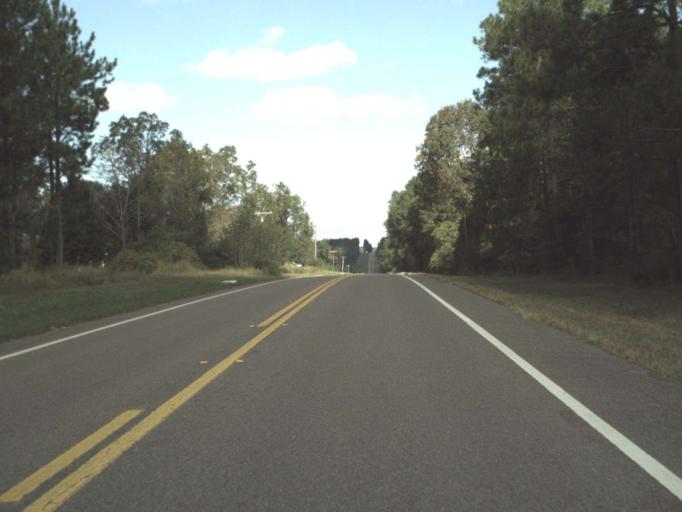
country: US
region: Florida
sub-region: Walton County
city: DeFuniak Springs
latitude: 30.8969
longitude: -86.1292
